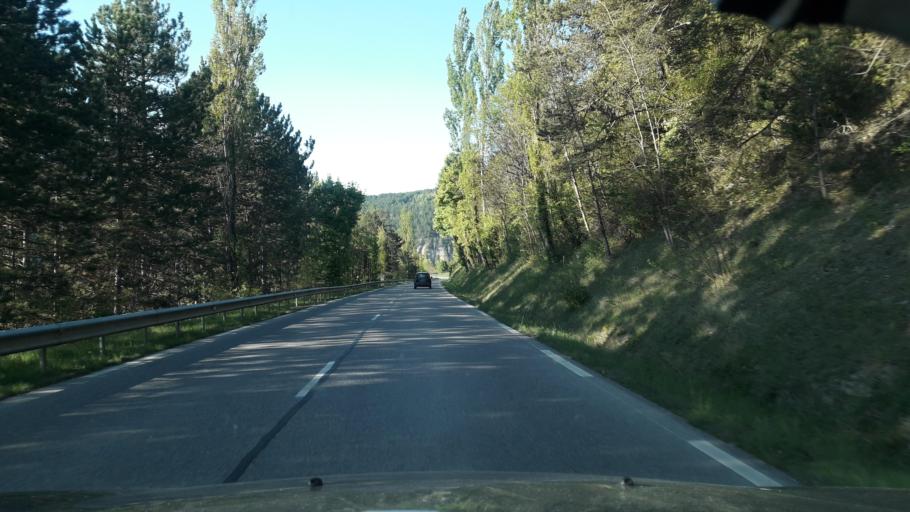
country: FR
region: Rhone-Alpes
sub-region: Departement de la Drome
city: Die
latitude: 44.7584
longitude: 5.2696
